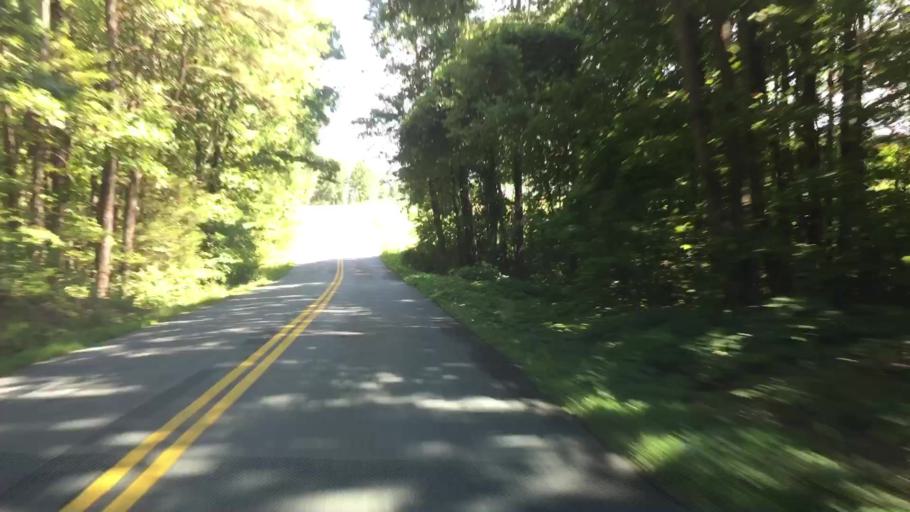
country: US
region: Virginia
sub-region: Appomattox County
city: Appomattox
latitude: 37.3160
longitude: -78.8451
